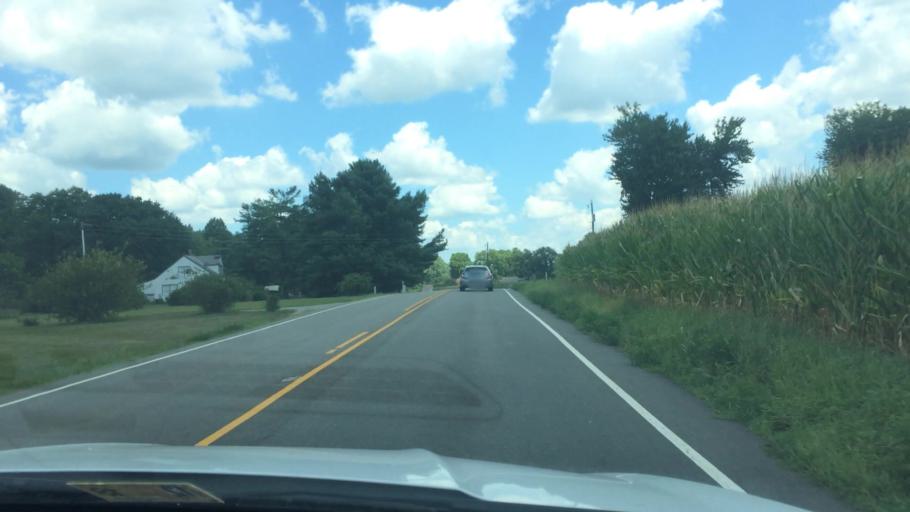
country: US
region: Virginia
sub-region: King William County
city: West Point
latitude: 37.5908
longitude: -76.7646
